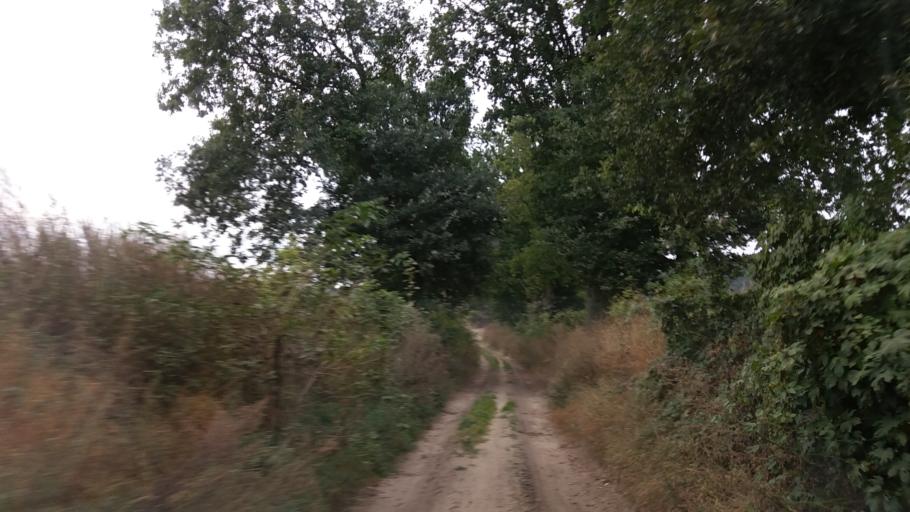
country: PL
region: West Pomeranian Voivodeship
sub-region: Powiat choszczenski
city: Pelczyce
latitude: 53.0828
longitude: 15.2958
